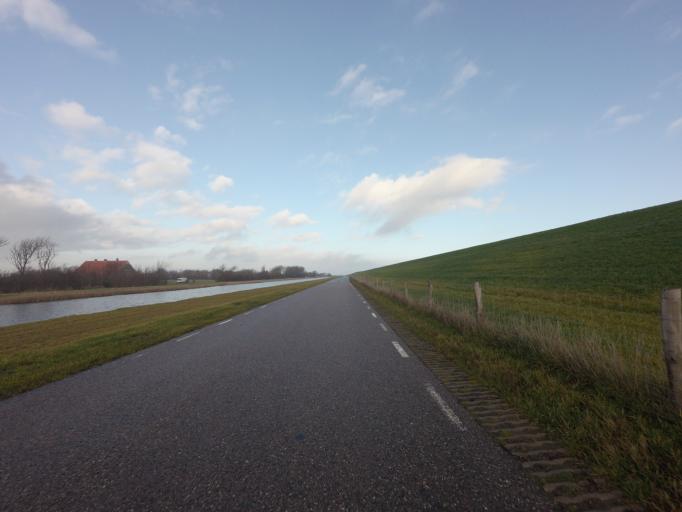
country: NL
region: North Holland
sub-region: Gemeente Texel
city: Den Burg
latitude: 53.1107
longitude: 4.8982
